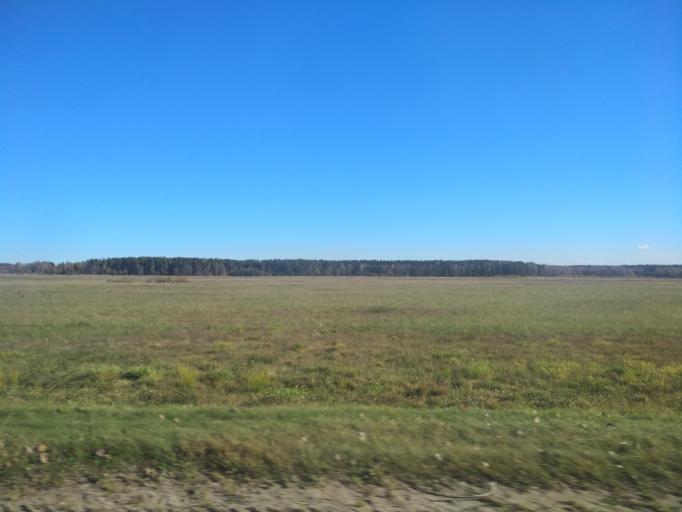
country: BY
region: Minsk
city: Il'ya
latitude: 54.5573
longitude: 27.2134
